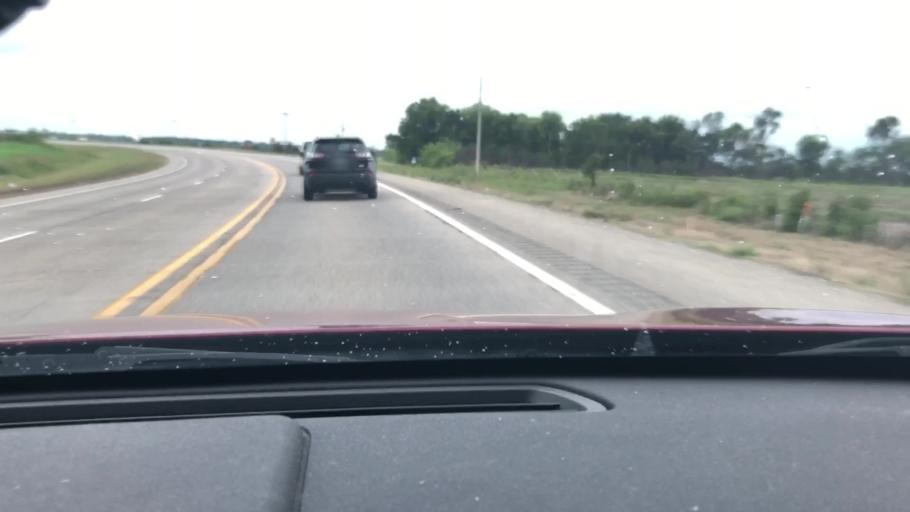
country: US
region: Arkansas
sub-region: Lafayette County
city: Lewisville
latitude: 33.3986
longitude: -93.7446
